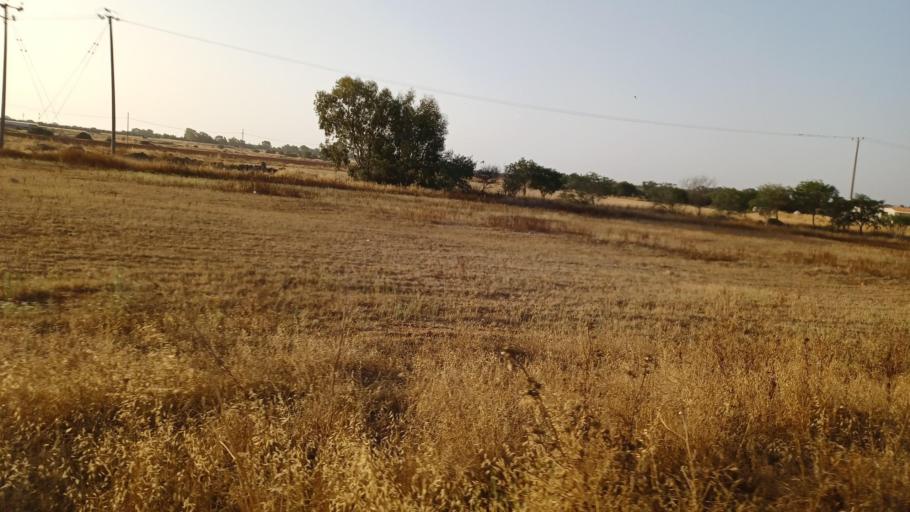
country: CY
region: Ammochostos
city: Liopetri
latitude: 34.9840
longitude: 33.8825
